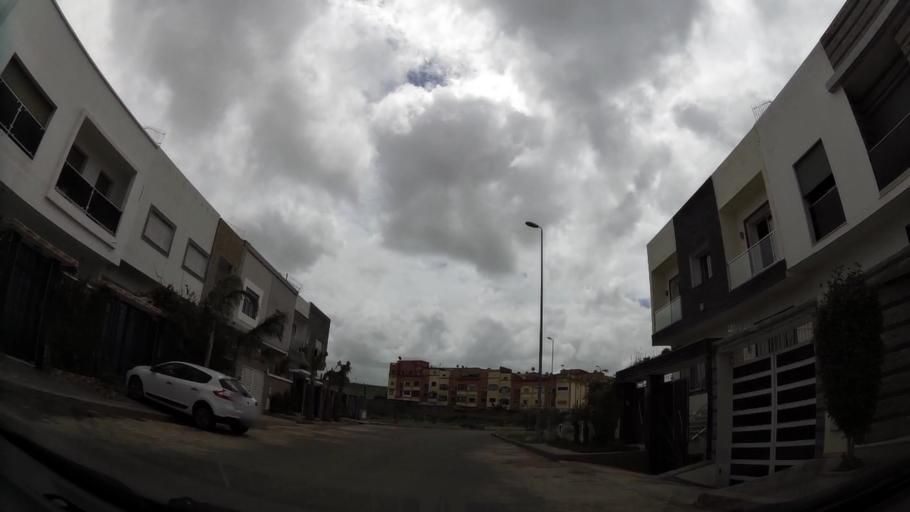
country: MA
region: Grand Casablanca
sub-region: Casablanca
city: Casablanca
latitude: 33.5306
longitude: -7.5967
